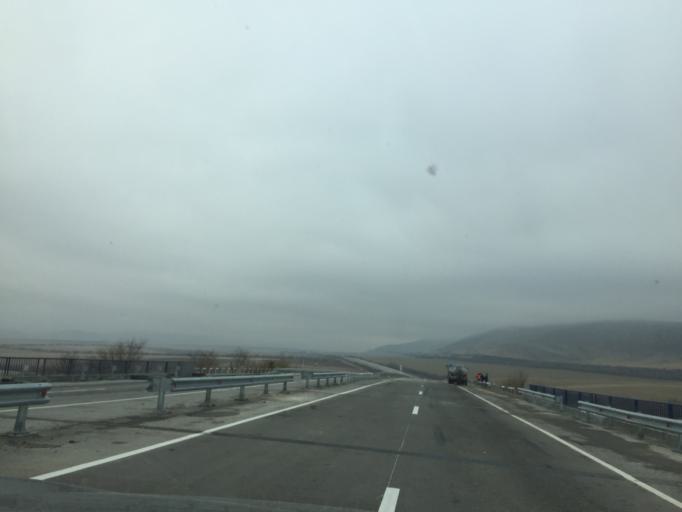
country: KZ
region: Ongtustik Qazaqstan
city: Sastobe
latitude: 42.5412
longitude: 70.0336
